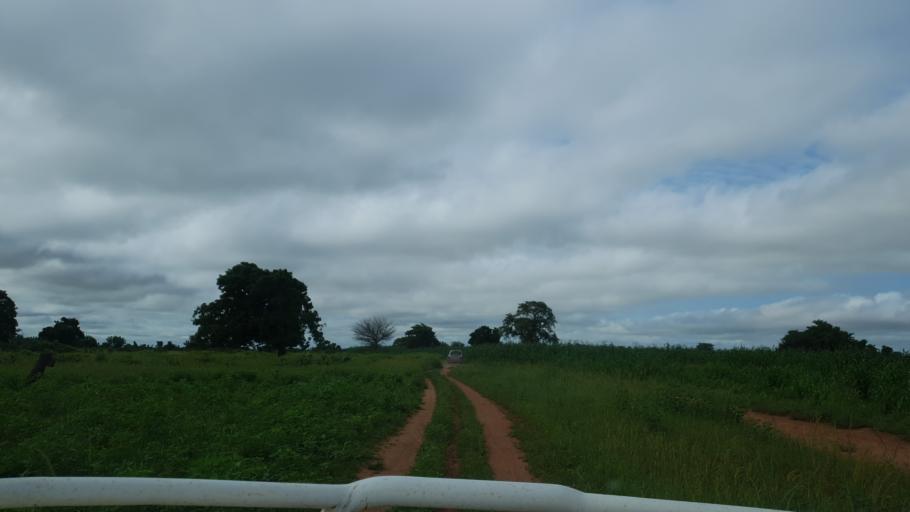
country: ML
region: Segou
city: Baroueli
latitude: 13.4996
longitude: -6.8975
